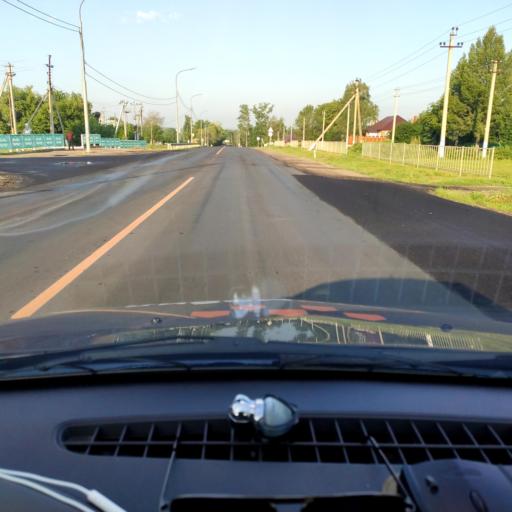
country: RU
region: Lipetsk
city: Izmalkovo
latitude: 52.4920
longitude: 38.0498
